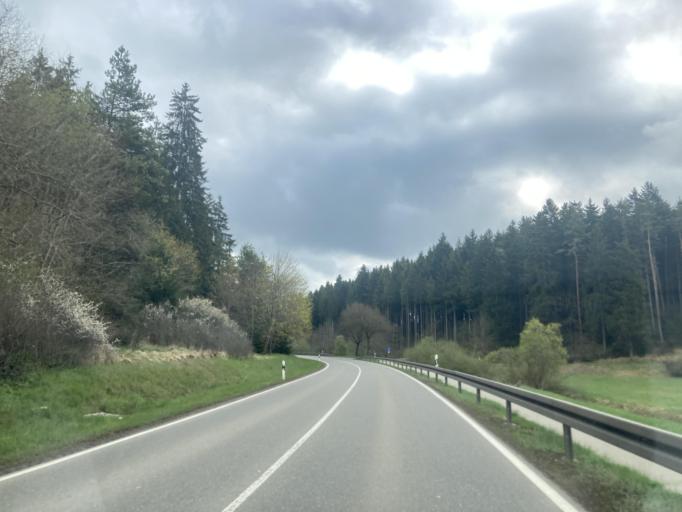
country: DE
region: Baden-Wuerttemberg
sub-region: Freiburg Region
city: Villingen-Schwenningen
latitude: 48.0310
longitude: 8.4906
